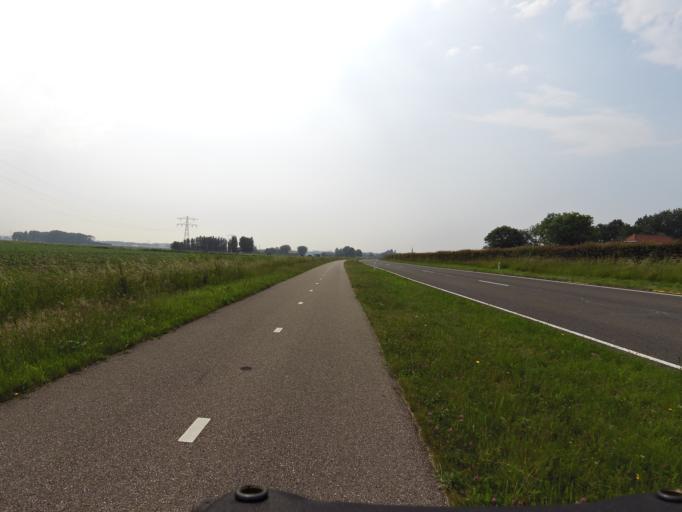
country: NL
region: South Holland
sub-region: Gemeente Spijkenisse
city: Spijkenisse
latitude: 51.8587
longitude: 4.2738
